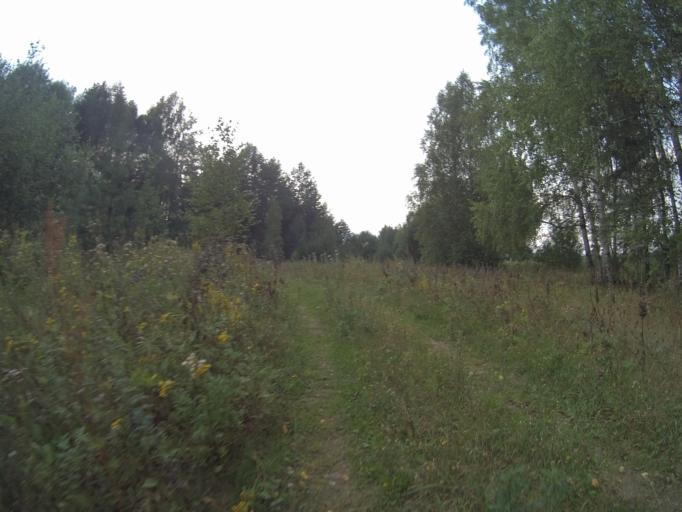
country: RU
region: Vladimir
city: Raduzhnyy
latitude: 55.9931
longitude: 40.2677
